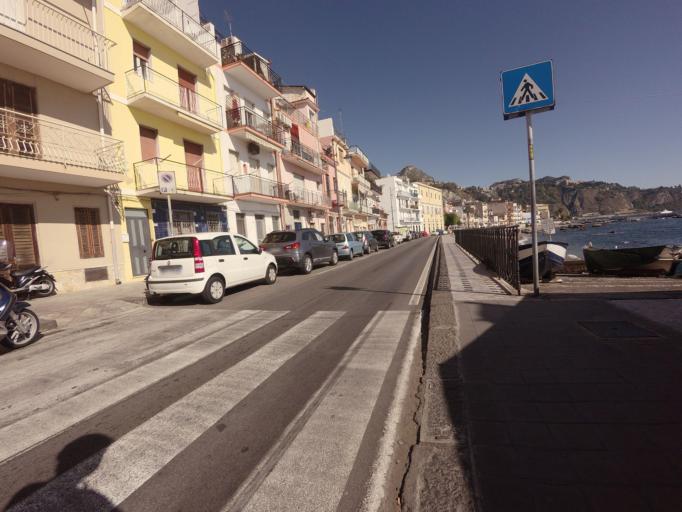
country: IT
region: Sicily
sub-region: Messina
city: Giardini-Naxos
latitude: 37.8393
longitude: 15.2767
